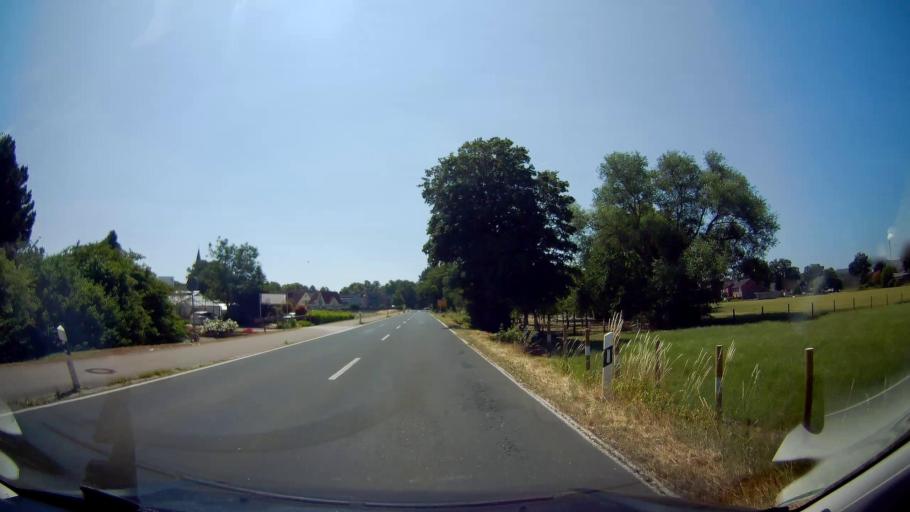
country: DE
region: North Rhine-Westphalia
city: Marl
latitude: 51.6285
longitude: 7.0491
